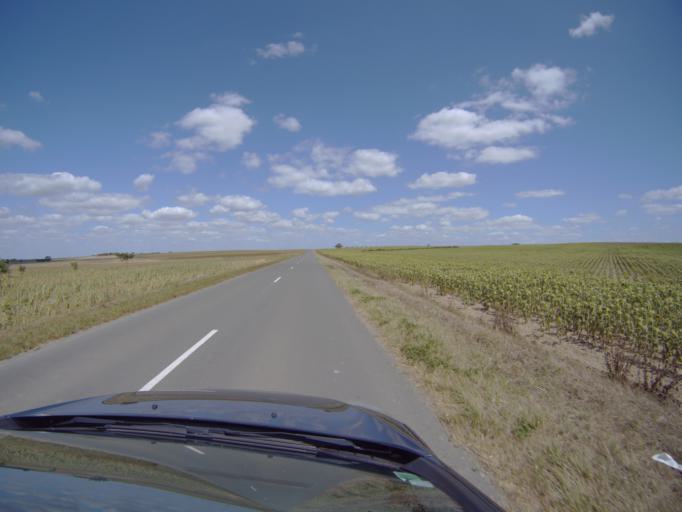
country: FR
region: Poitou-Charentes
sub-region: Departement des Deux-Sevres
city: Saint-Hilaire-la-Palud
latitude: 46.2614
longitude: -0.6948
